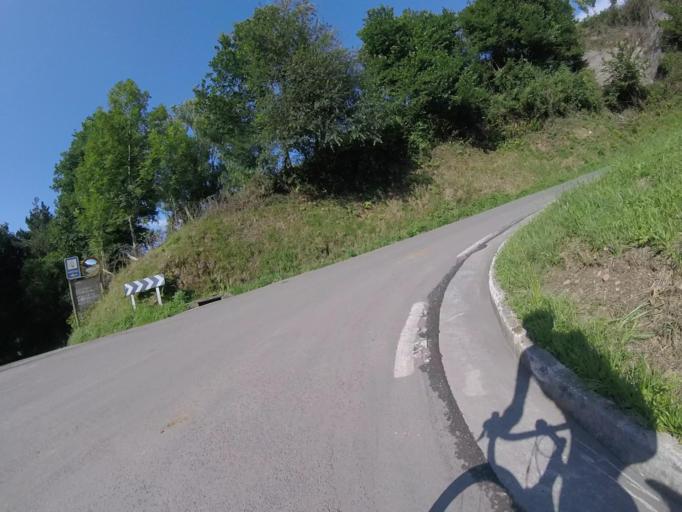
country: ES
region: Basque Country
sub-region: Provincia de Guipuzcoa
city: Zizurkil
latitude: 43.1839
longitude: -2.0829
